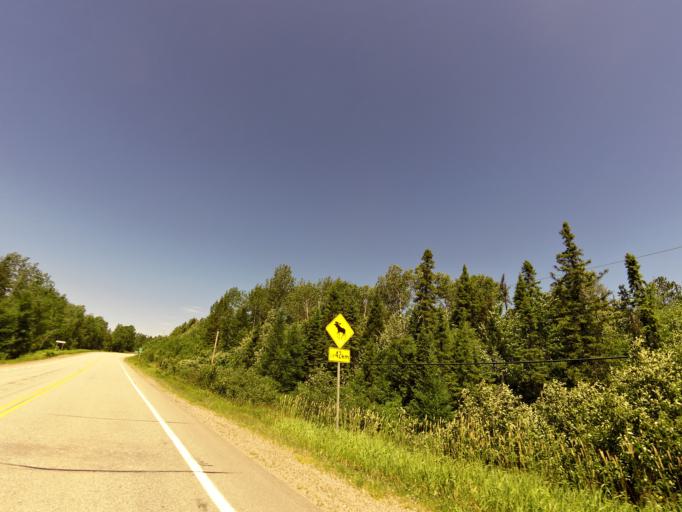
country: CA
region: Quebec
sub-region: Abitibi-Temiscamingue
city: Temiscaming
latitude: 46.7488
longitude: -79.0736
